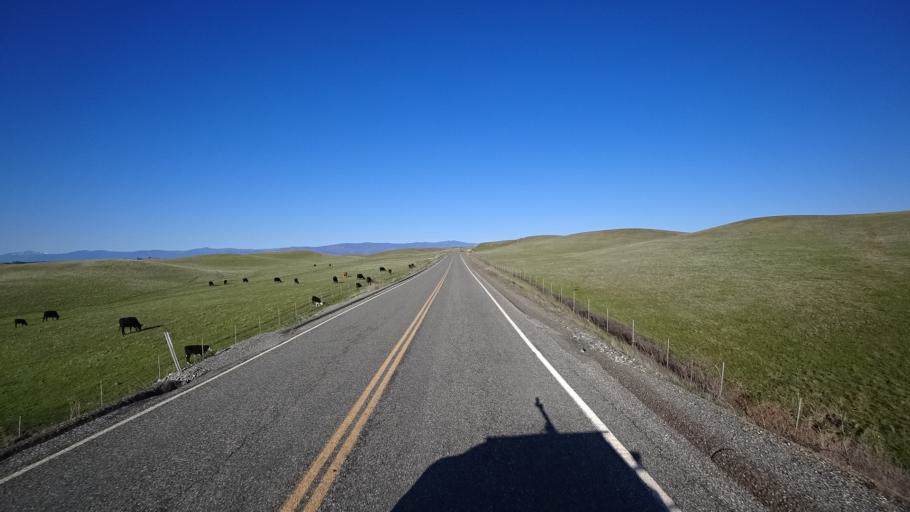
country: US
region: California
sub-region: Glenn County
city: Orland
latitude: 39.8286
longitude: -122.3620
